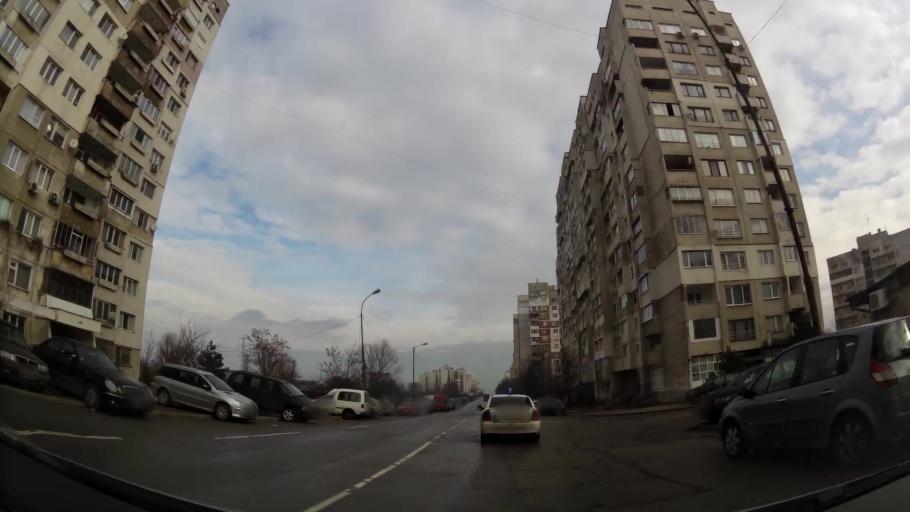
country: BG
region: Sofiya
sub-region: Obshtina Bozhurishte
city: Bozhurishte
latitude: 42.7163
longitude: 23.2370
